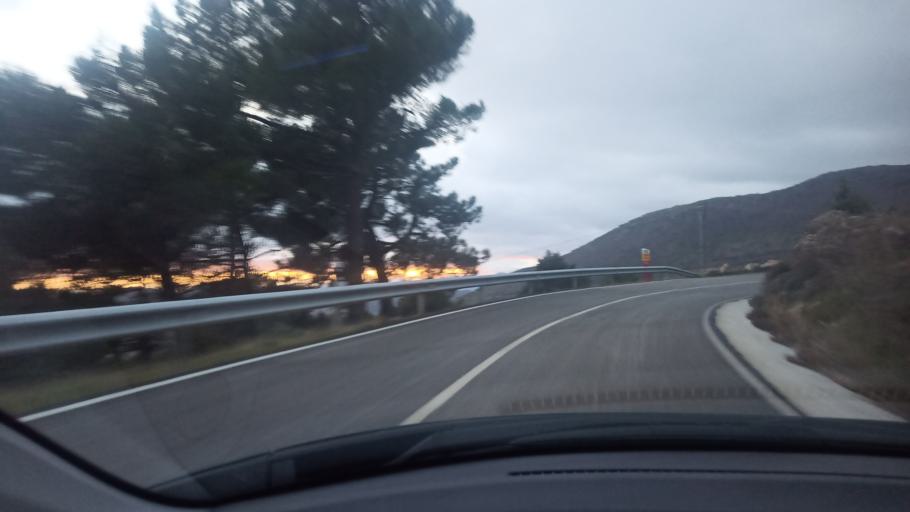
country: ES
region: Madrid
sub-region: Provincia de Madrid
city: Zarzalejo
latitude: 40.5514
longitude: -4.1941
